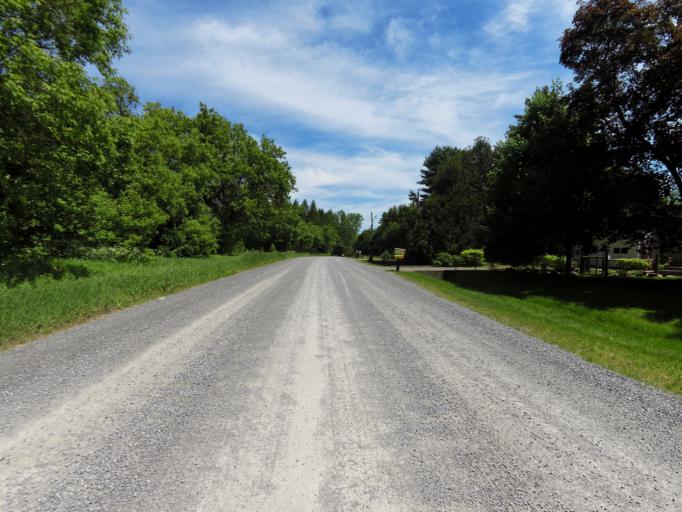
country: CA
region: Ontario
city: Ottawa
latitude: 45.3414
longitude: -75.6158
